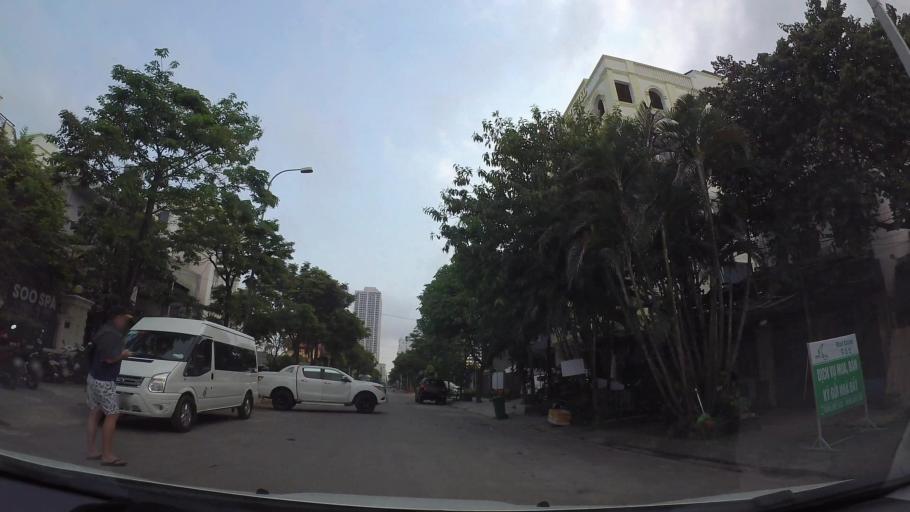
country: VN
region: Da Nang
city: Son Tra
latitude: 16.0586
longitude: 108.2448
